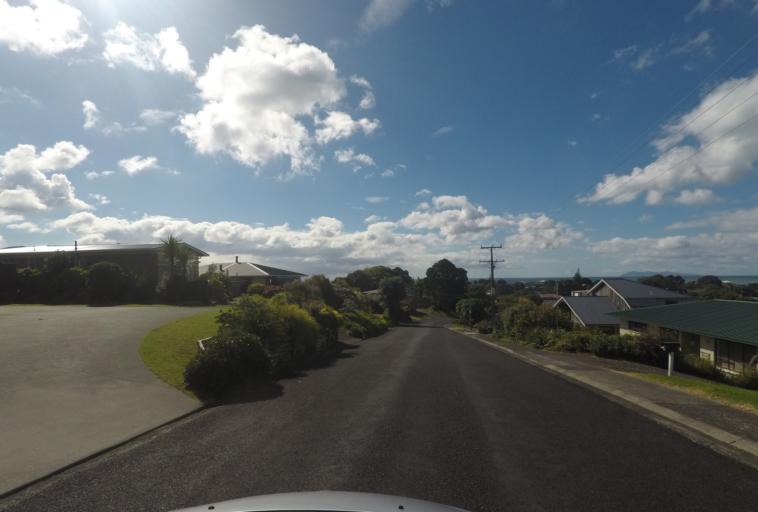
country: NZ
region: Bay of Plenty
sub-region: Western Bay of Plenty District
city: Waihi Beach
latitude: -37.4120
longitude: 175.9387
